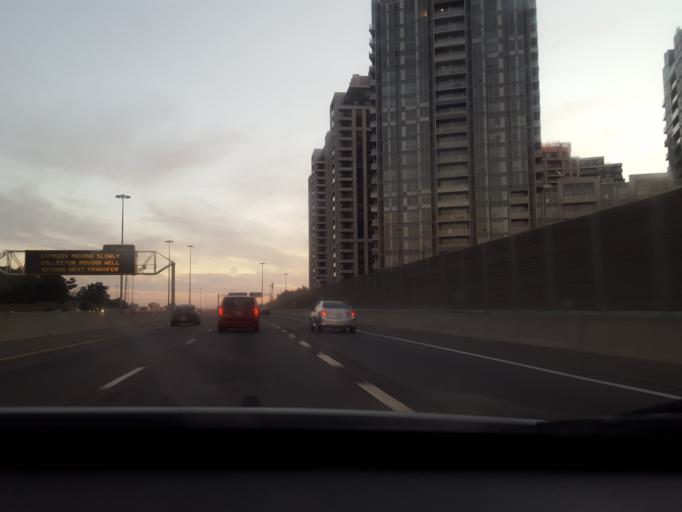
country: CA
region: Ontario
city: Willowdale
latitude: 43.7584
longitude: -79.4012
